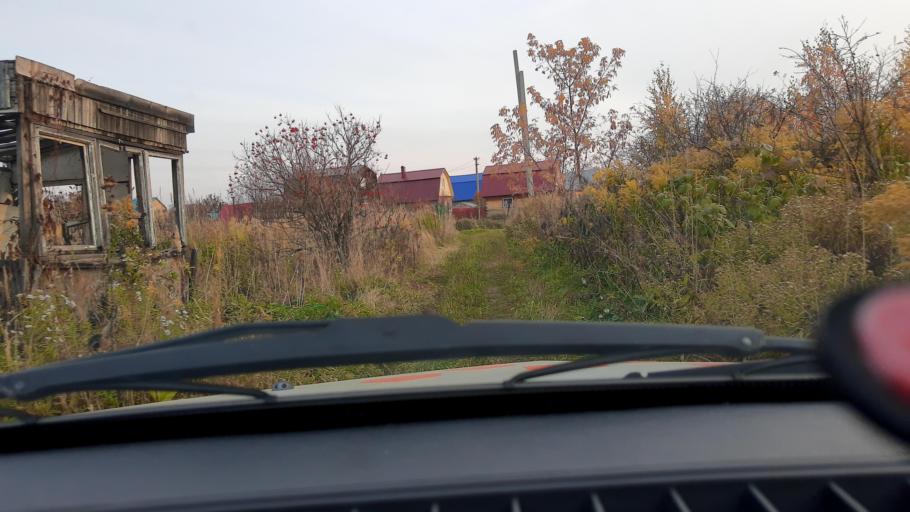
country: RU
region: Bashkortostan
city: Iglino
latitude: 54.8038
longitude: 56.3500
